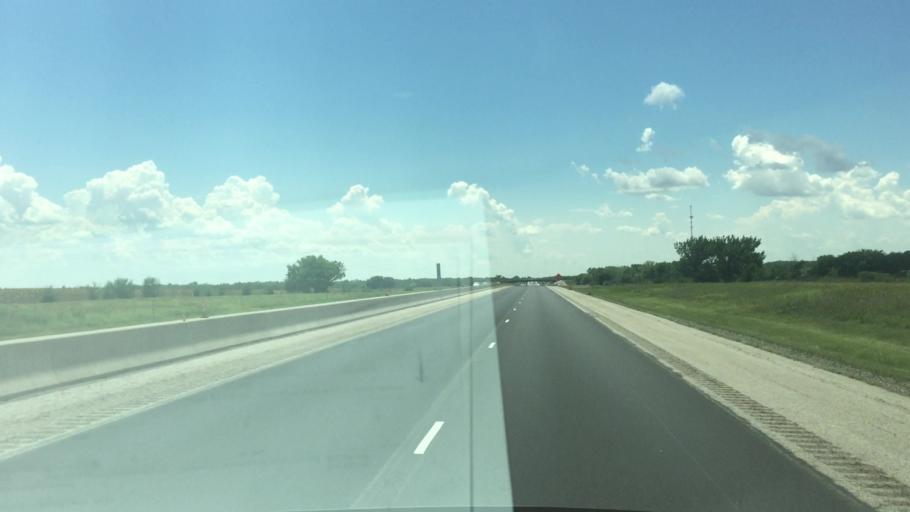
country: US
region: Kansas
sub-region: Osage County
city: Osage City
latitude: 38.7456
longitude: -95.9467
